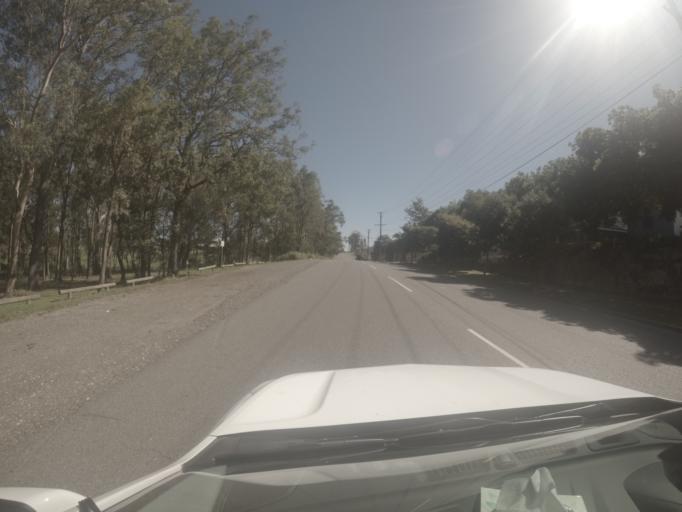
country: AU
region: Queensland
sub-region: Brisbane
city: Richlands
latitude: -27.5765
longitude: 152.9602
